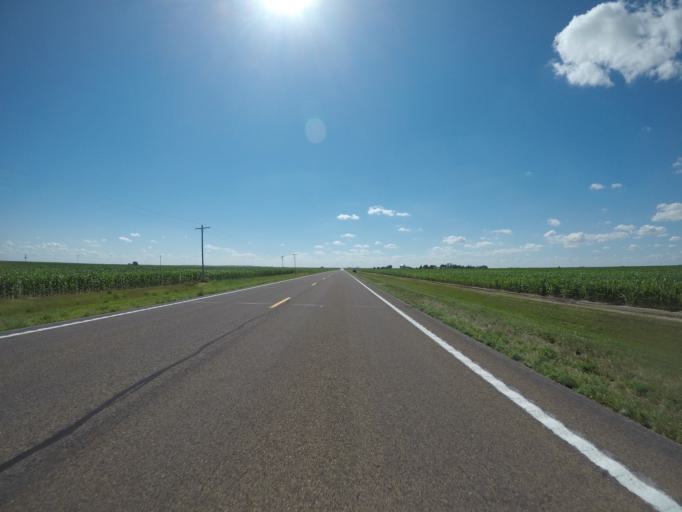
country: US
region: Nebraska
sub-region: Chase County
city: Imperial
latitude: 40.5375
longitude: -101.9385
